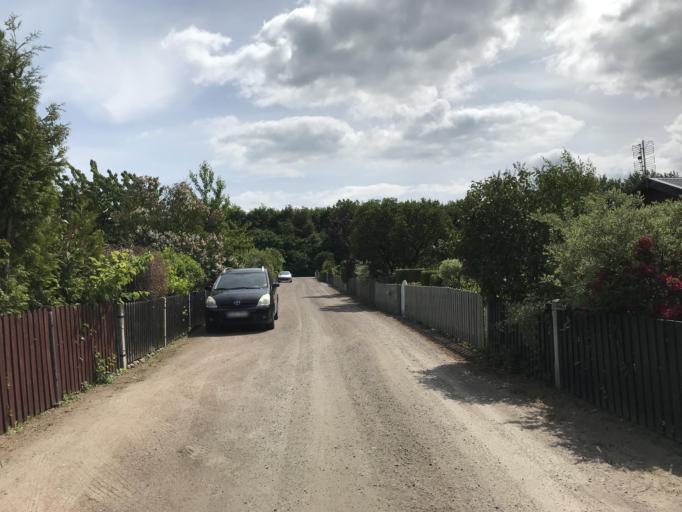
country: SE
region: Skane
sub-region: Landskrona
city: Landskrona
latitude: 55.8970
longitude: 12.8418
